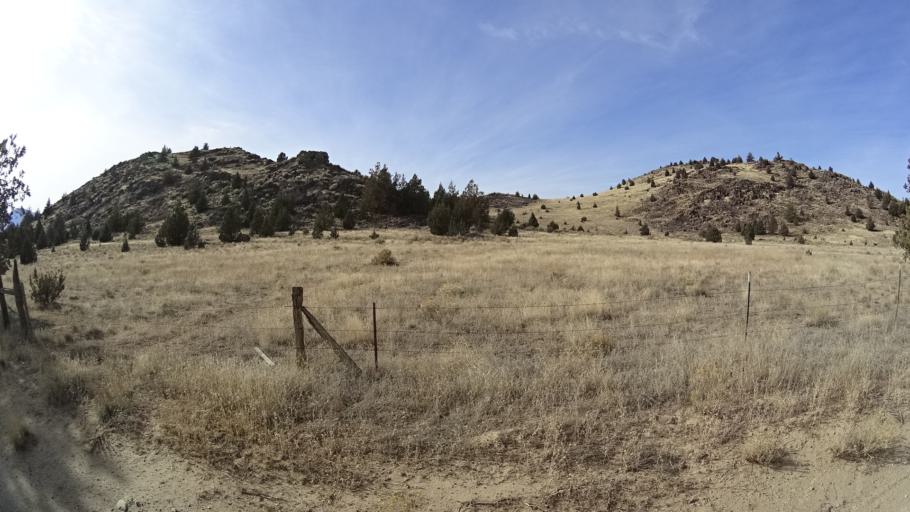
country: US
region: California
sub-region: Siskiyou County
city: Weed
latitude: 41.5657
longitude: -122.4680
